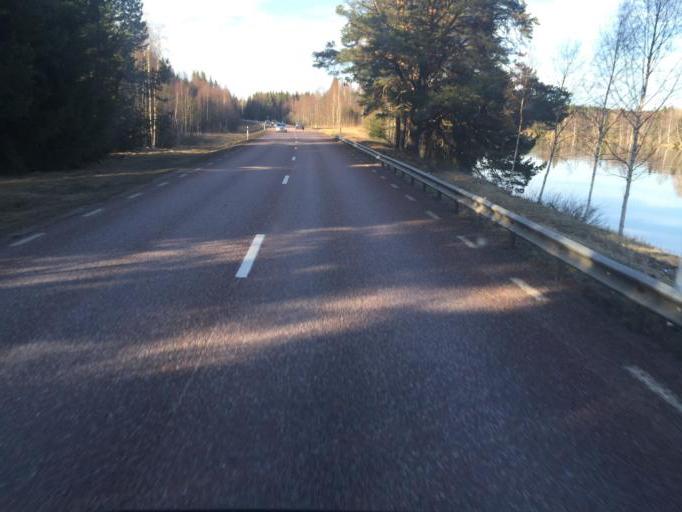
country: SE
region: Dalarna
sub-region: Gagnefs Kommun
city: Mockfjard
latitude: 60.4687
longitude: 14.7676
